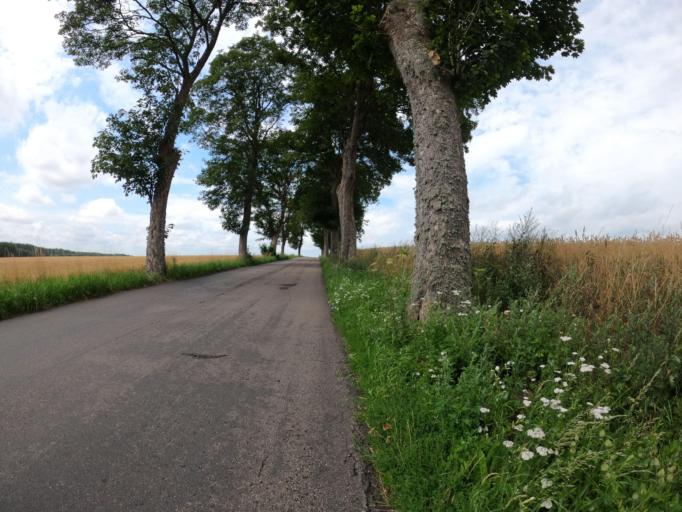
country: PL
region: West Pomeranian Voivodeship
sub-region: Powiat szczecinecki
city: Grzmiaca
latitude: 53.7873
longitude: 16.4868
